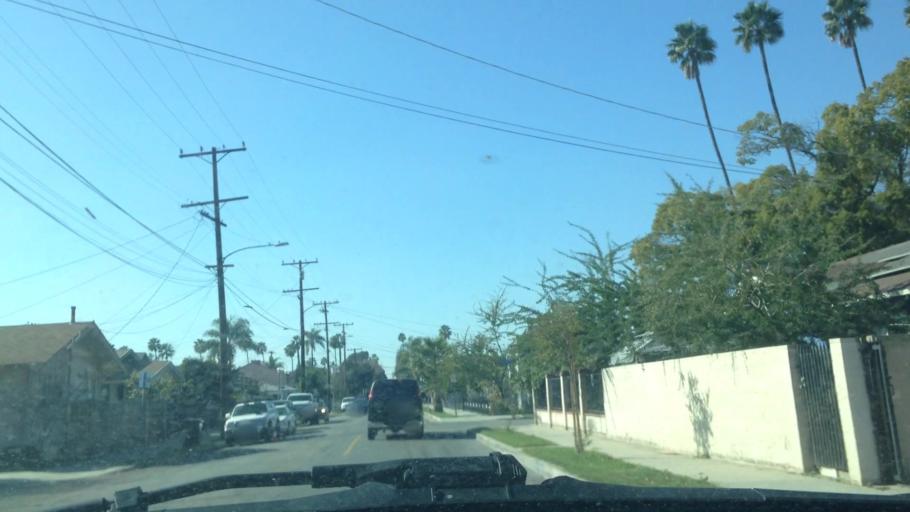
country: US
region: California
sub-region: Orange County
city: Anaheim
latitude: 33.8406
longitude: -117.9123
